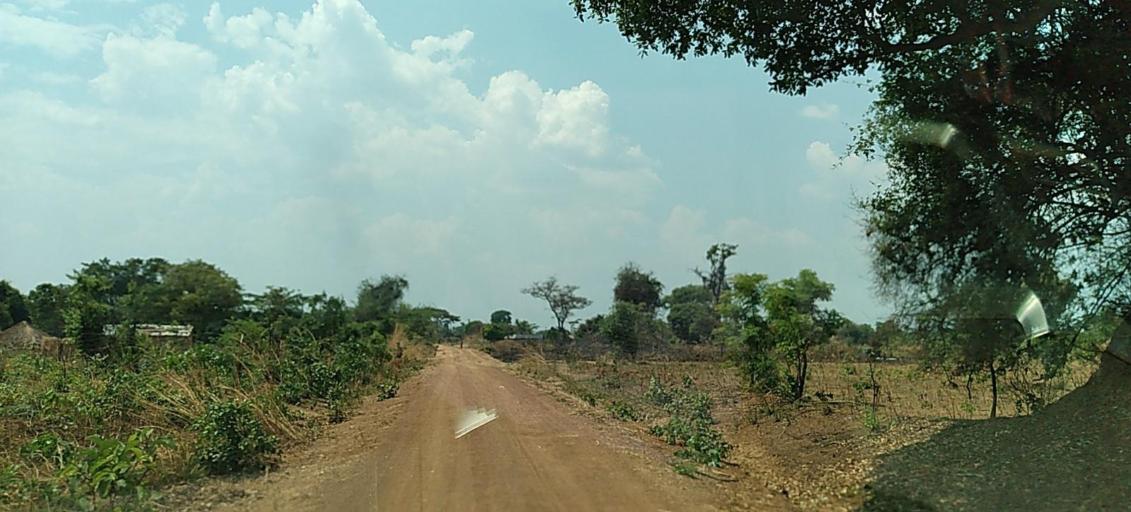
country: ZM
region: Copperbelt
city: Chingola
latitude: -12.5957
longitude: 27.7121
